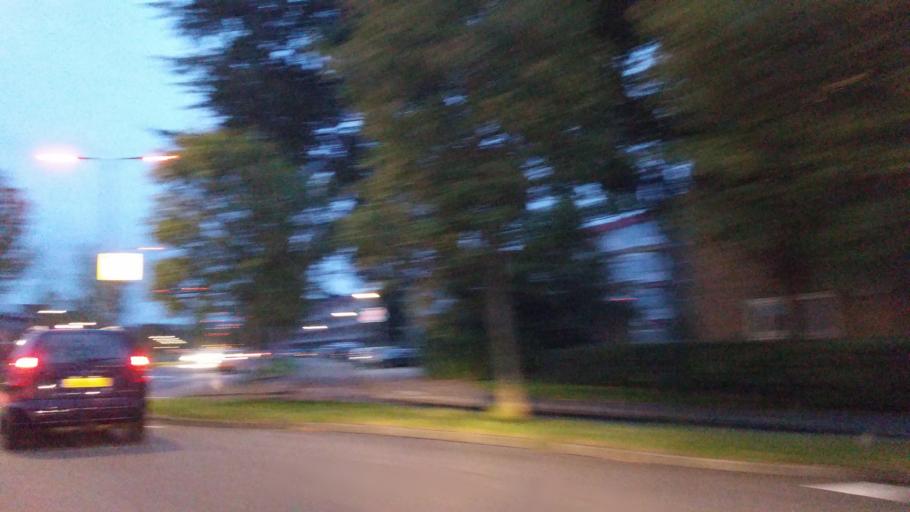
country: NL
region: Friesland
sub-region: Gemeente Leeuwarden
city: Bilgaard
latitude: 53.2127
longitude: 5.8034
